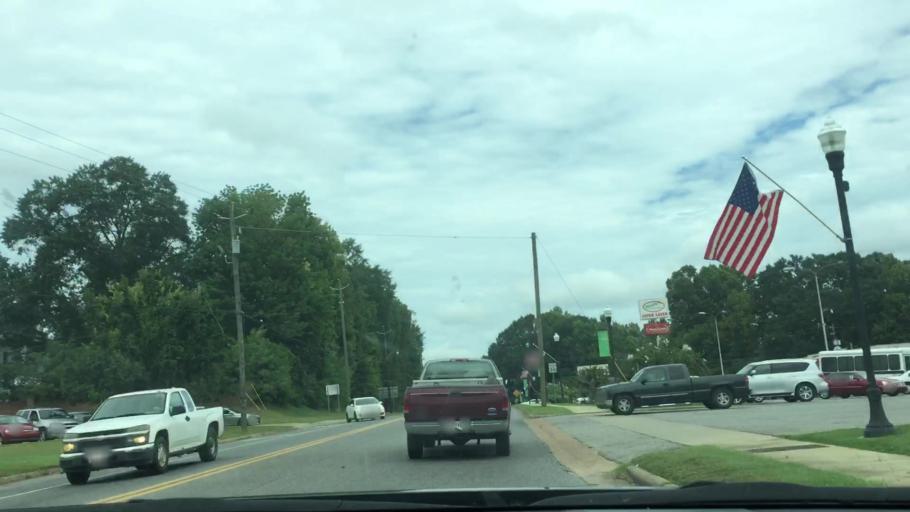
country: US
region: Alabama
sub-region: Hale County
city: Greensboro
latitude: 32.6995
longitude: -87.5953
